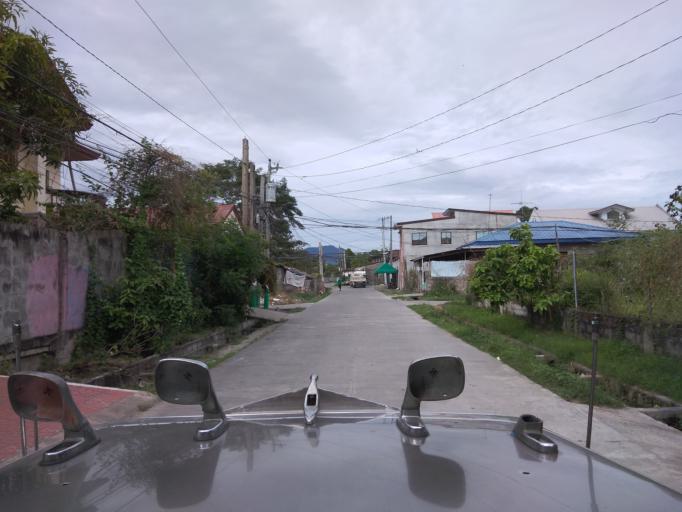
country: PH
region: Central Luzon
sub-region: Province of Pampanga
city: Mexico
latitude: 15.0630
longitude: 120.7252
